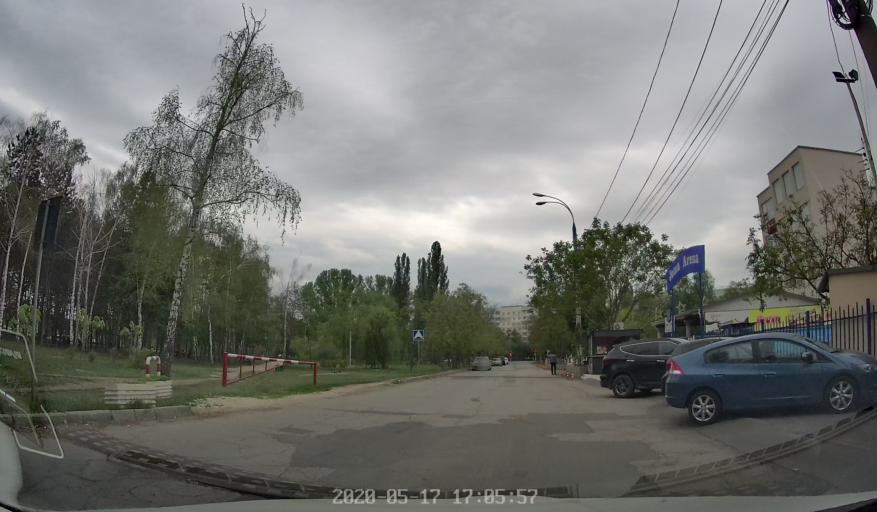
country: MD
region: Chisinau
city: Vatra
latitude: 47.0476
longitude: 28.7838
